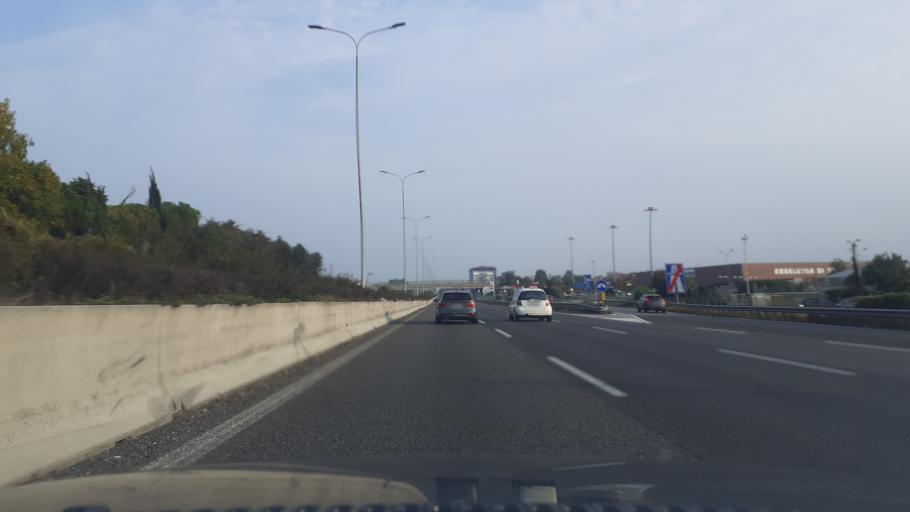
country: IT
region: Lombardy
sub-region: Provincia di Monza e Brianza
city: Santa Margherita
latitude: 45.6455
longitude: 9.2255
